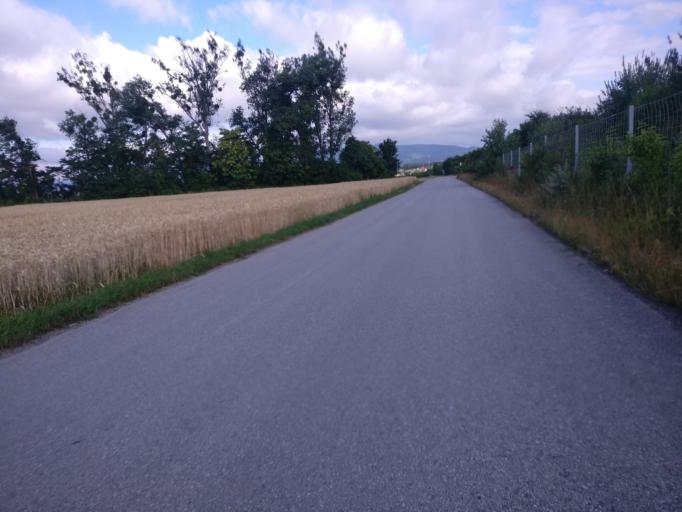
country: AT
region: Lower Austria
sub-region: Politischer Bezirk Baden
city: Trumau
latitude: 48.0258
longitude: 16.3470
